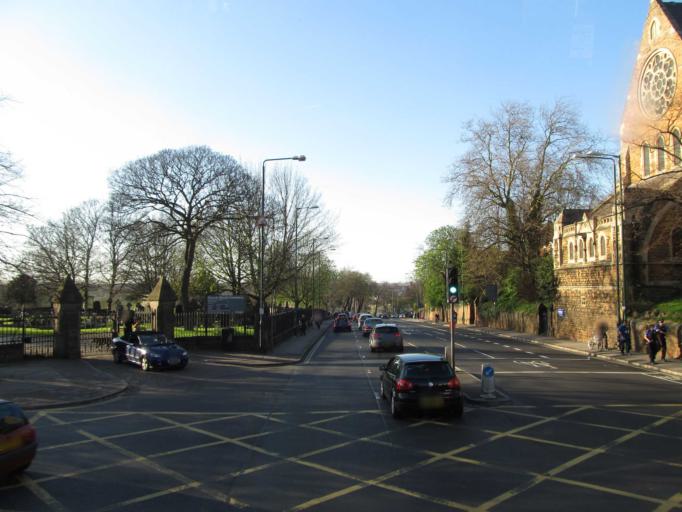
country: GB
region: England
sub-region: Nottingham
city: Nottingham
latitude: 52.9646
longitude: -1.1527
